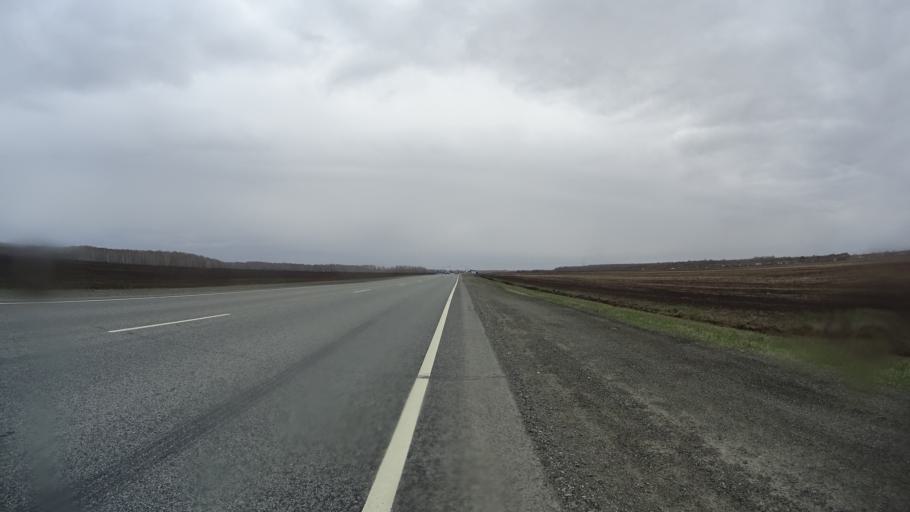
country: RU
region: Chelyabinsk
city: Krasnogorskiy
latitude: 54.5852
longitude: 61.2909
